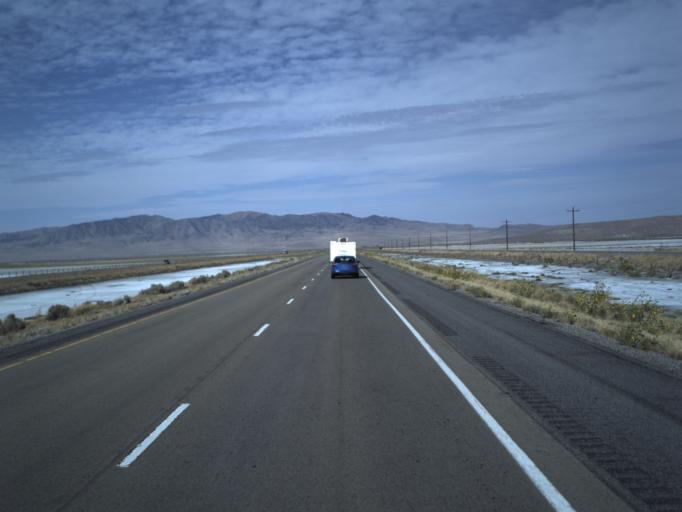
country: US
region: Utah
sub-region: Tooele County
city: Grantsville
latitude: 40.7511
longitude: -112.7023
